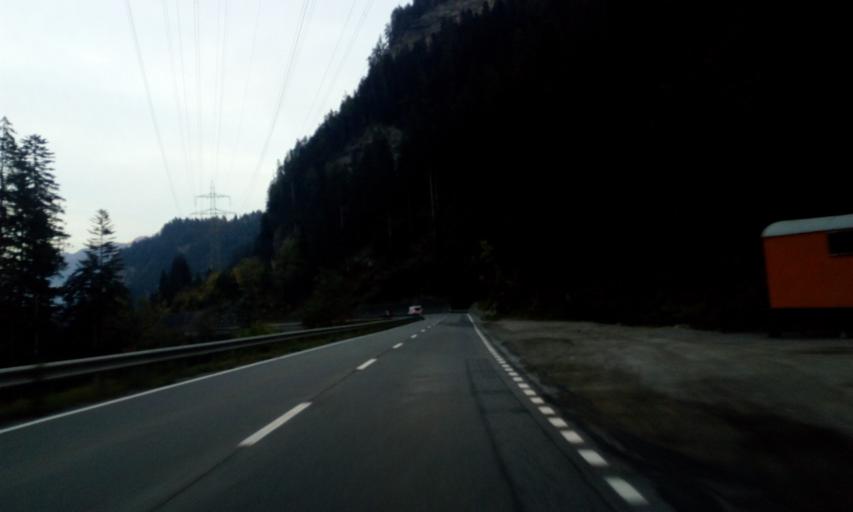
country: CH
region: Grisons
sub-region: Hinterrhein District
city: Thusis
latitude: 46.6927
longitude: 9.4933
